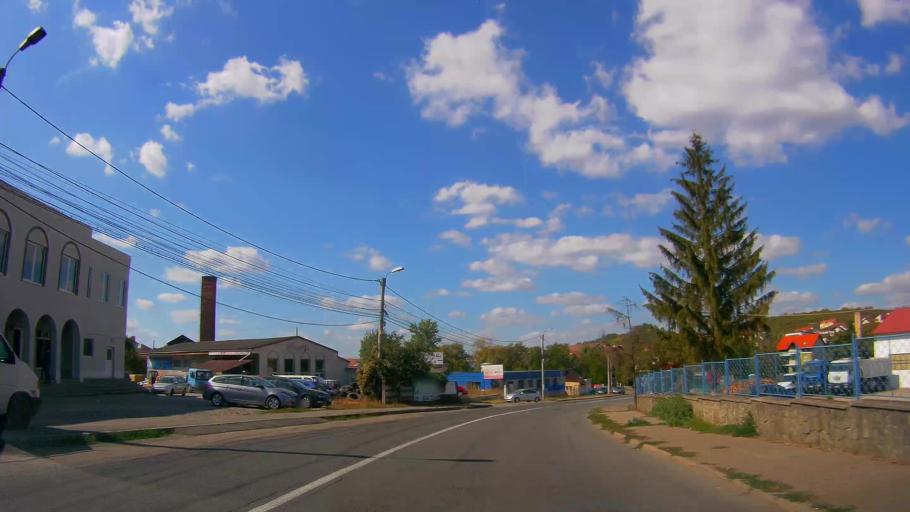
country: RO
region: Salaj
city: Zalau
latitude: 47.1729
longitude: 23.0723
